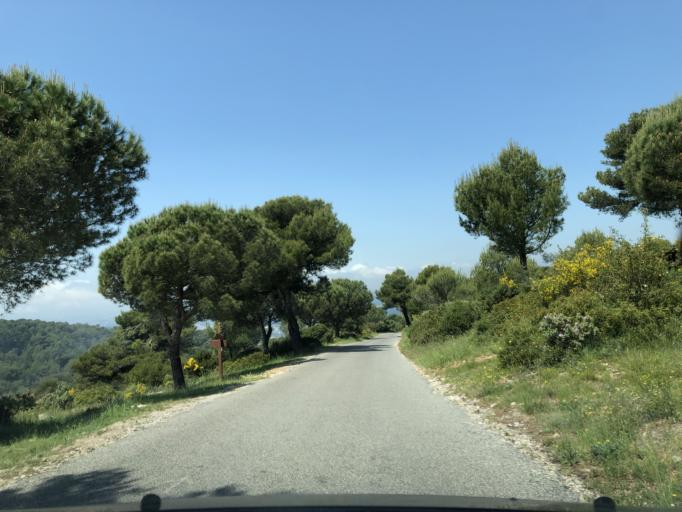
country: FR
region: Provence-Alpes-Cote d'Azur
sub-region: Departement des Alpes-Maritimes
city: Eze
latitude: 43.7384
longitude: 7.3524
